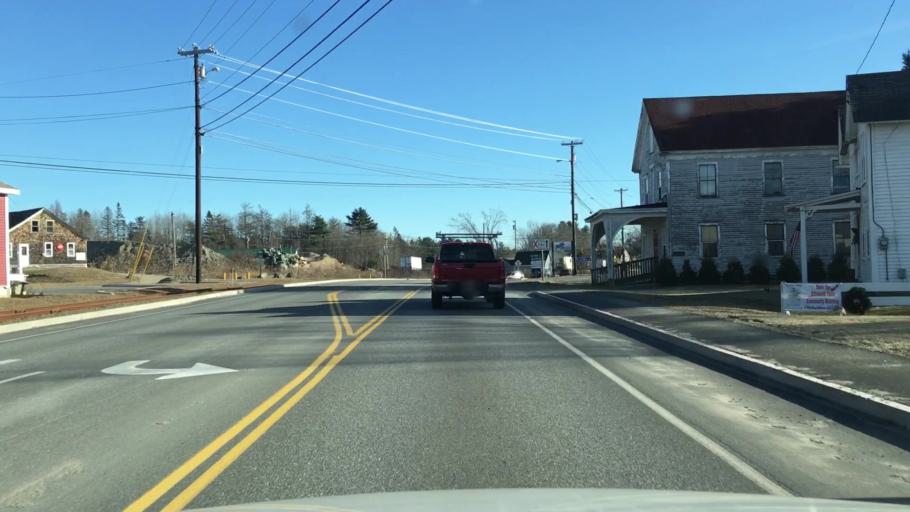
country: US
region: Maine
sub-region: Hancock County
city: Ellsworth
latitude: 44.5625
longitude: -68.4396
